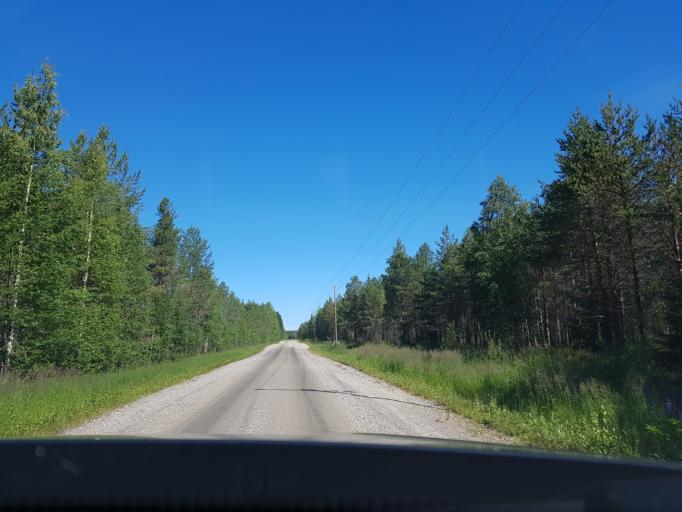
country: FI
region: Kainuu
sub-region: Kehys-Kainuu
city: Kuhmo
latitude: 64.1846
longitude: 29.5957
